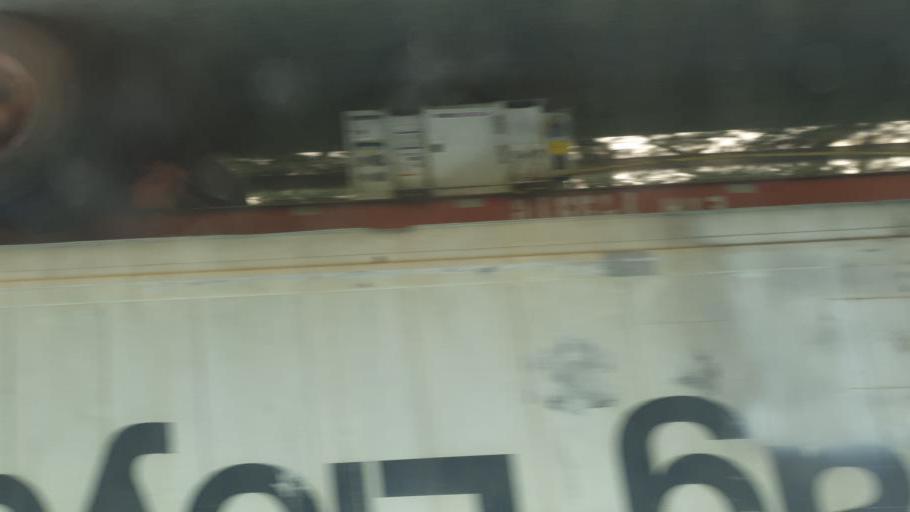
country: DO
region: Santiago
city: Santiago de los Caballeros
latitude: 19.4256
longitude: -70.6806
